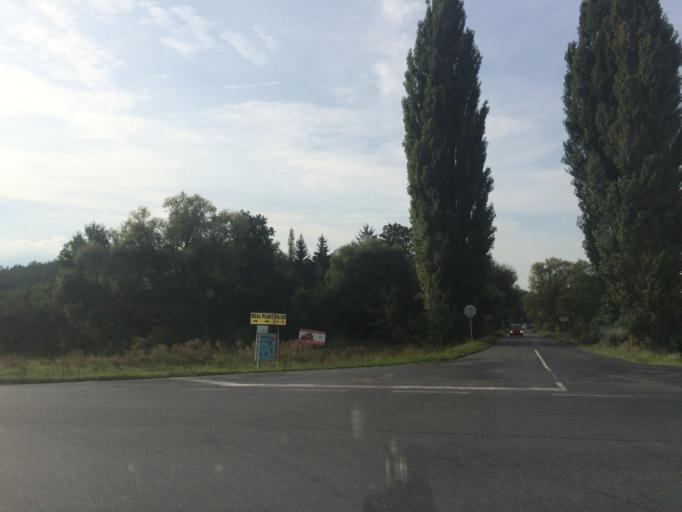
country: CZ
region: Central Bohemia
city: Cesky Brod
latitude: 50.0606
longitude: 14.8790
